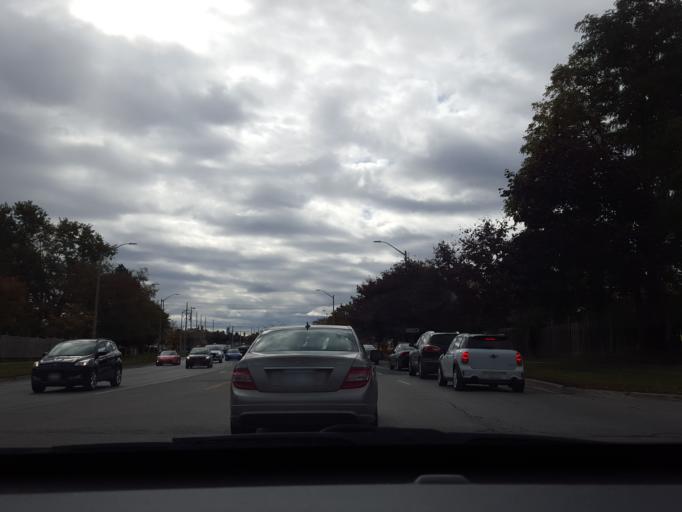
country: CA
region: Ontario
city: Markham
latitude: 43.8644
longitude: -79.3044
